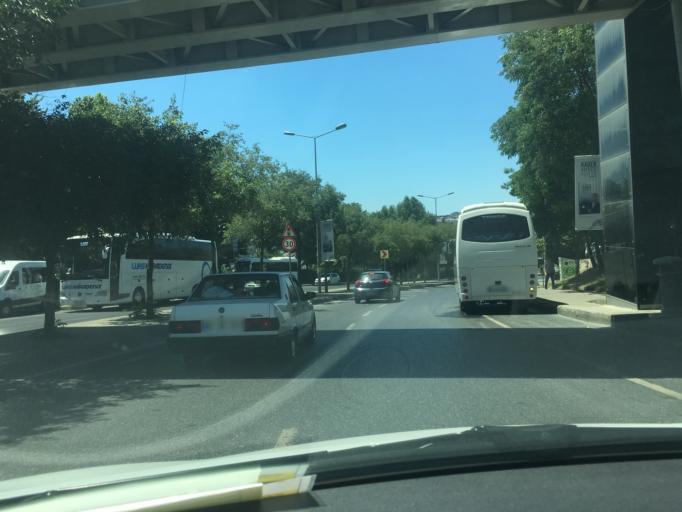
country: TR
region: Istanbul
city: Istanbul
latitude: 41.0499
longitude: 28.9464
